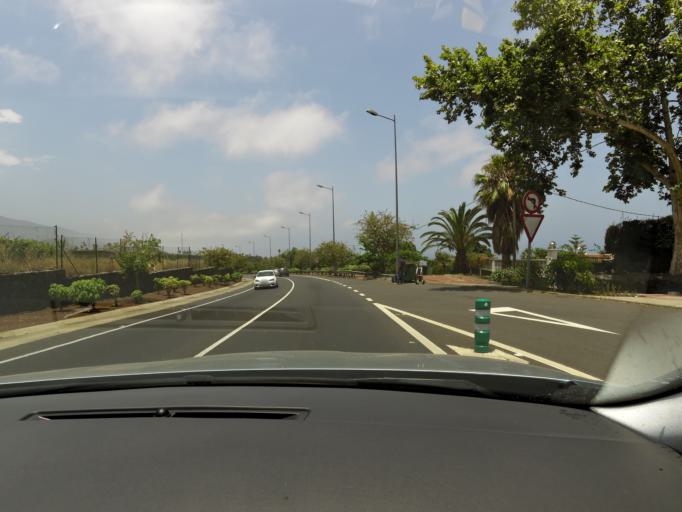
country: ES
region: Canary Islands
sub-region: Provincia de Santa Cruz de Tenerife
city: La Orotava
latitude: 28.4054
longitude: -16.5234
